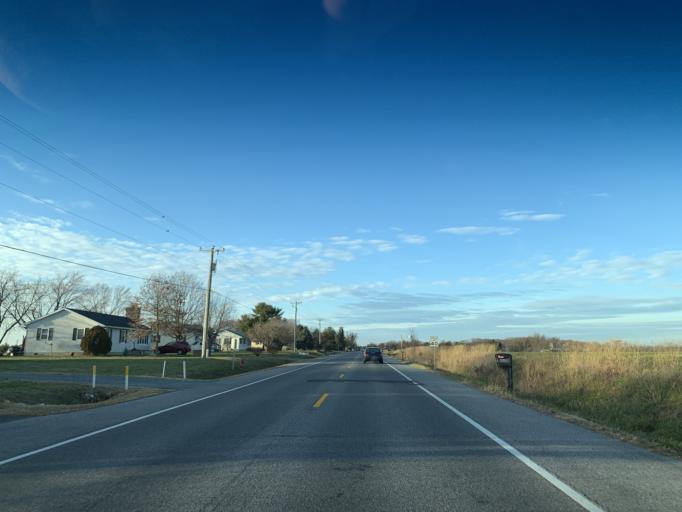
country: US
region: Maryland
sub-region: Kent County
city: Chestertown
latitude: 39.2644
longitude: -76.0874
